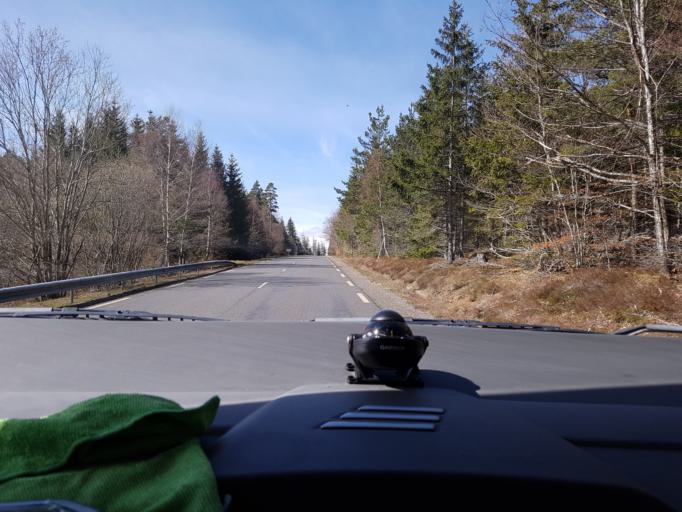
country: FR
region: Auvergne
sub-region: Departement du Cantal
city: Chaudes-Aigues
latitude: 44.7970
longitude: 2.9218
